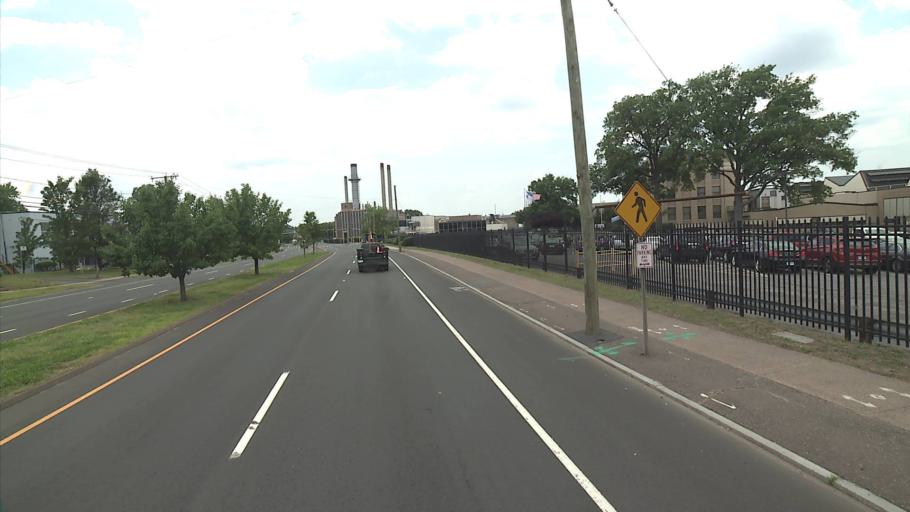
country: US
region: Connecticut
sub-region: Hartford County
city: Wethersfield
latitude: 41.7466
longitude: -72.6353
